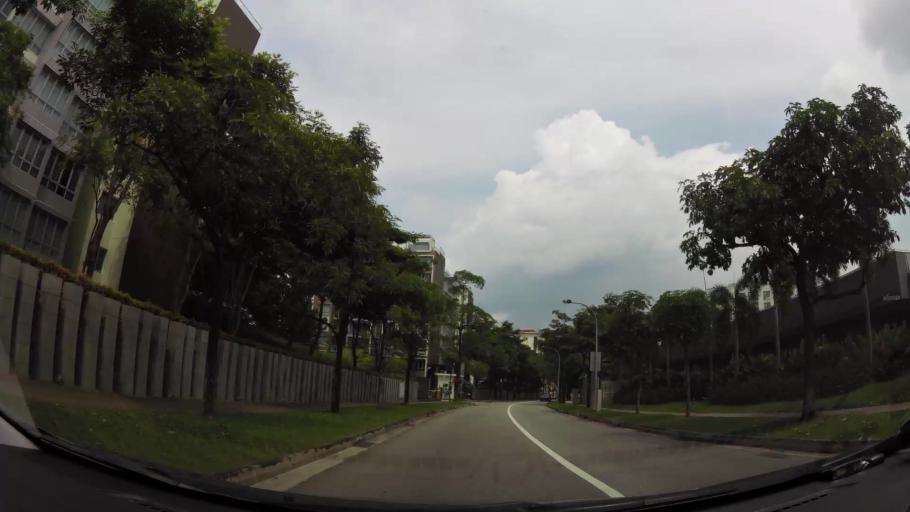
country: SG
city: Singapore
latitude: 1.3576
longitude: 103.9649
